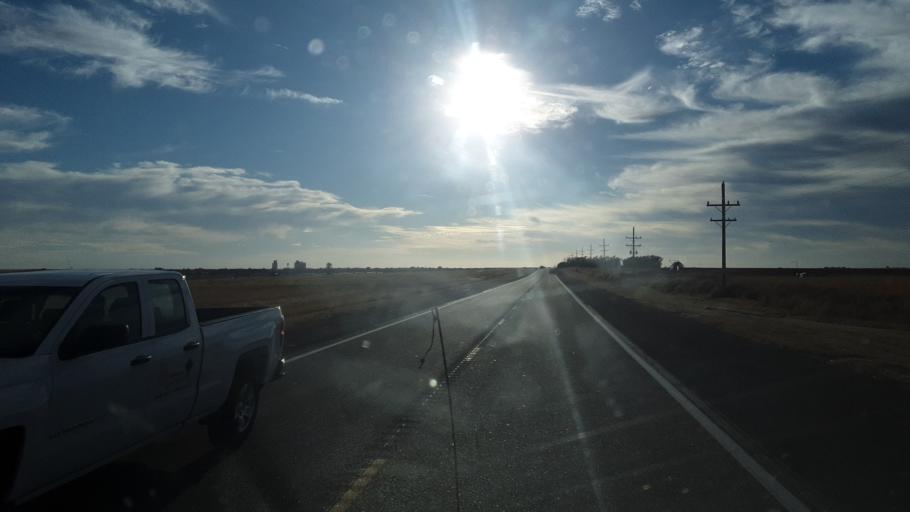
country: US
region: Kansas
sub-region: Kearny County
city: Lakin
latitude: 37.9576
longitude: -101.2317
